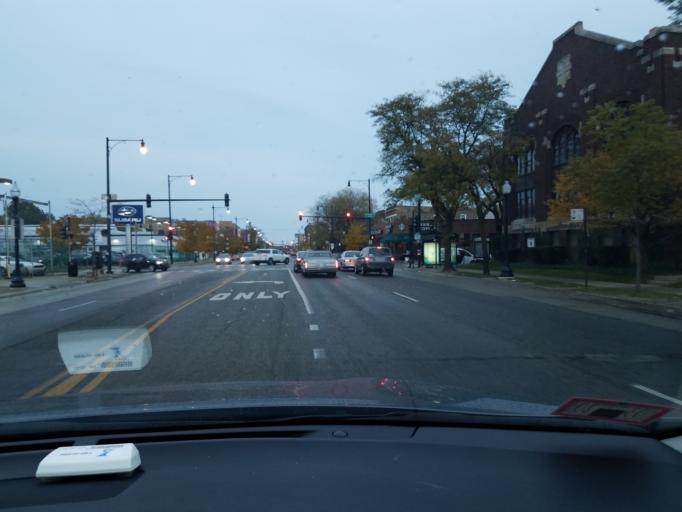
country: US
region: Illinois
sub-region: Cook County
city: Lincolnwood
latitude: 41.9535
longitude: -87.7387
